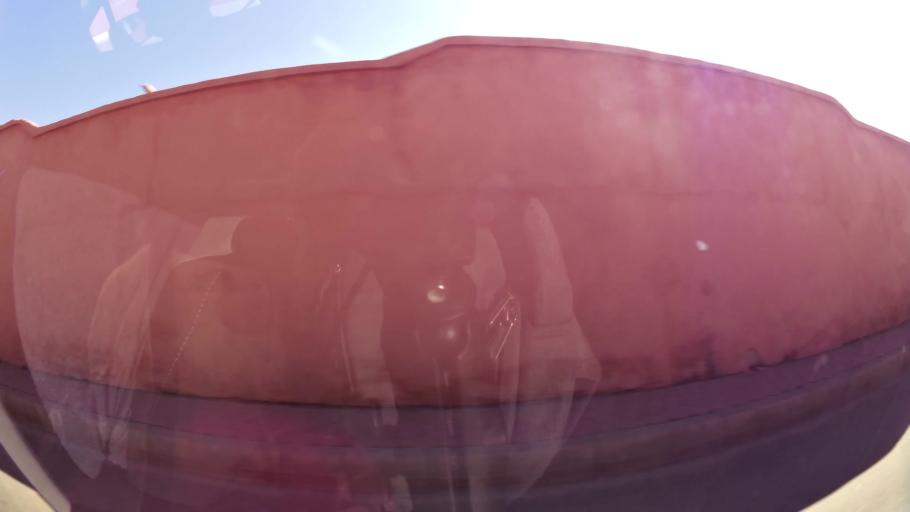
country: MA
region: Marrakech-Tensift-Al Haouz
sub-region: Marrakech
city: Marrakesh
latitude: 31.6365
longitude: -8.0046
